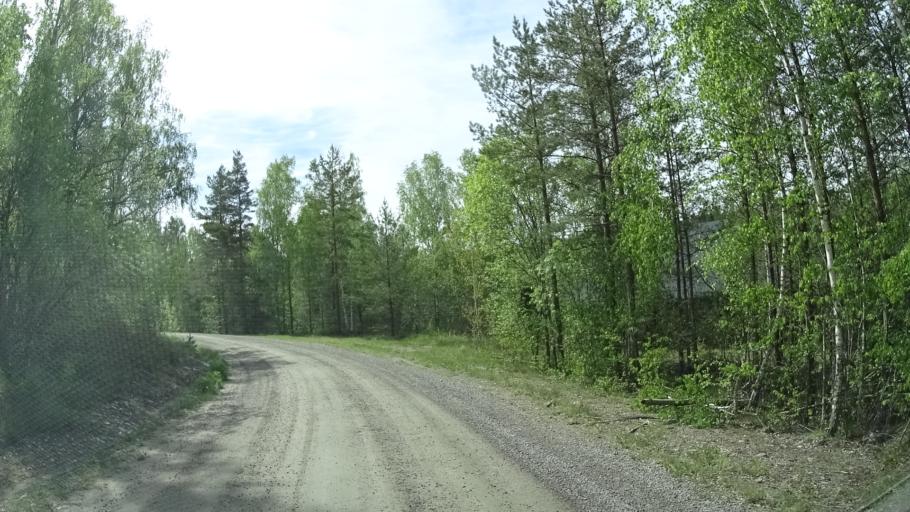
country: SE
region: OEstergoetland
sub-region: Finspangs Kommun
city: Finspang
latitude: 58.7536
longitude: 15.8299
